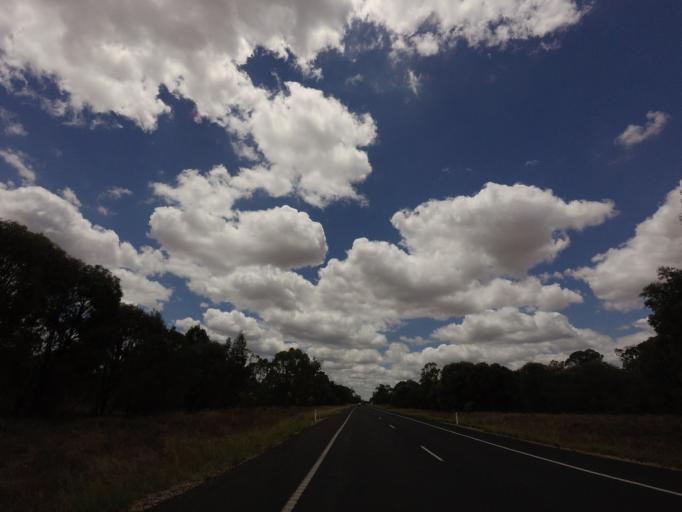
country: AU
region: Queensland
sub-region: Goondiwindi
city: Goondiwindi
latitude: -28.0735
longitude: 150.7479
